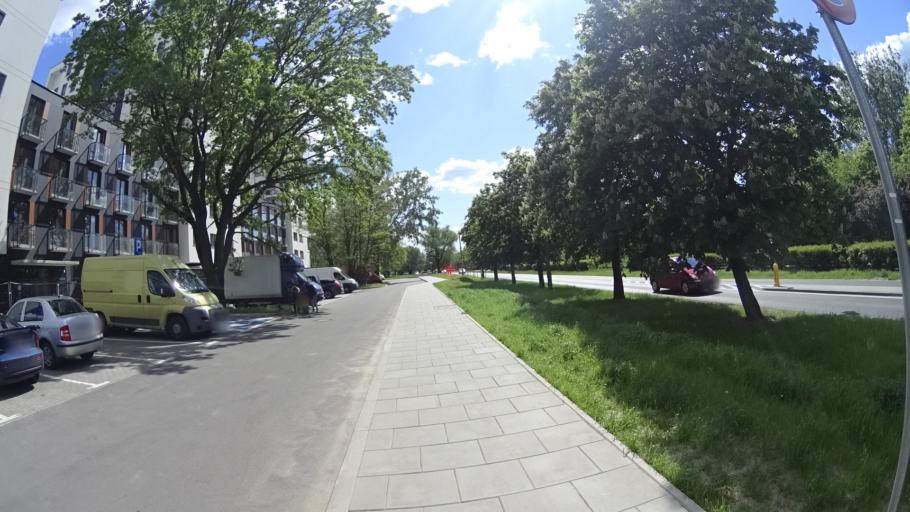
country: PL
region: Masovian Voivodeship
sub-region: Warszawa
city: Bielany
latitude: 52.2856
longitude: 20.9245
